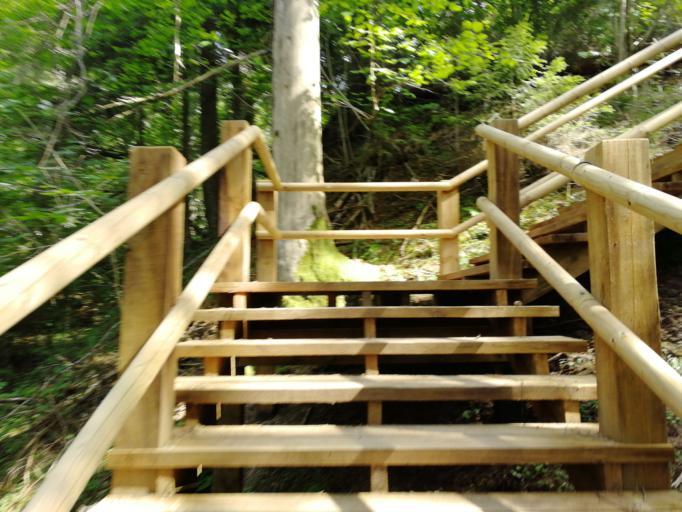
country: LV
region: Cesu Rajons
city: Cesis
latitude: 57.3028
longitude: 25.2210
